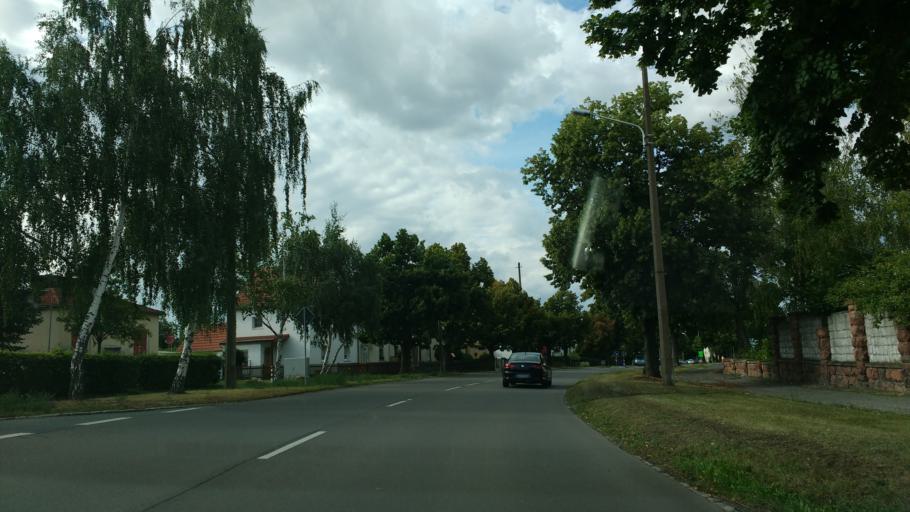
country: DE
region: Saxony-Anhalt
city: Zeitz
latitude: 51.0410
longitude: 12.1244
